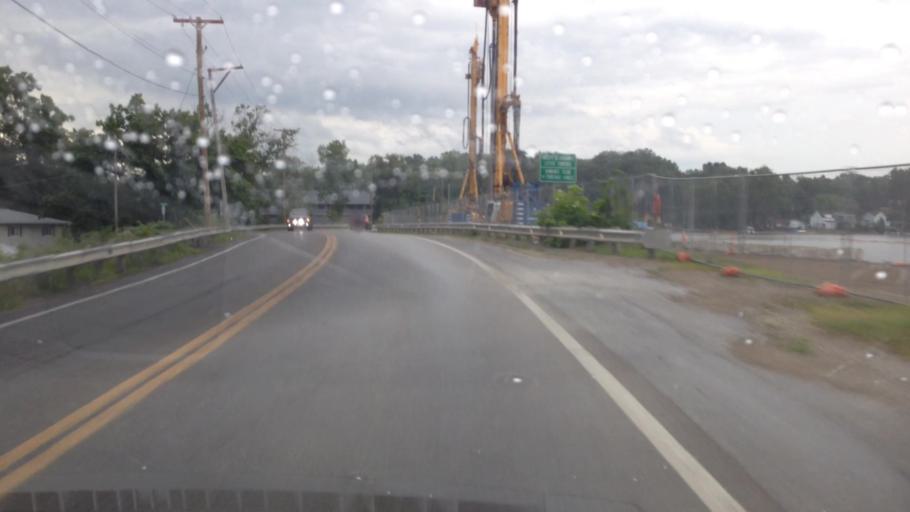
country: US
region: Ohio
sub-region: Summit County
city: Portage Lakes
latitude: 40.9979
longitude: -81.5333
